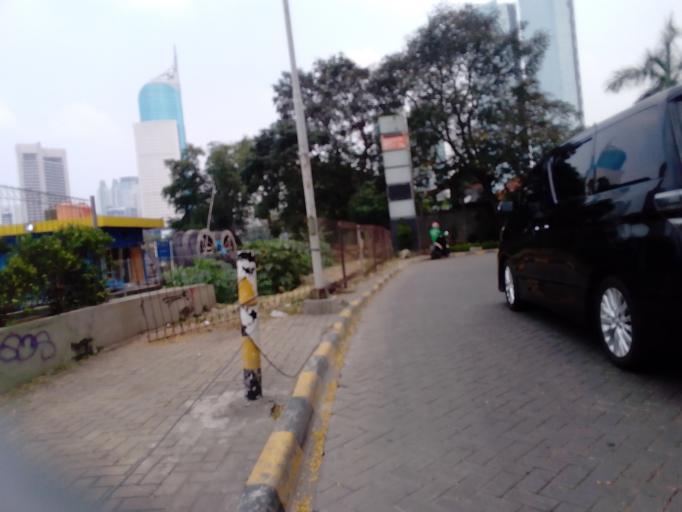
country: ID
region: Jakarta Raya
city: Jakarta
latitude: -6.1978
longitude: 106.8175
